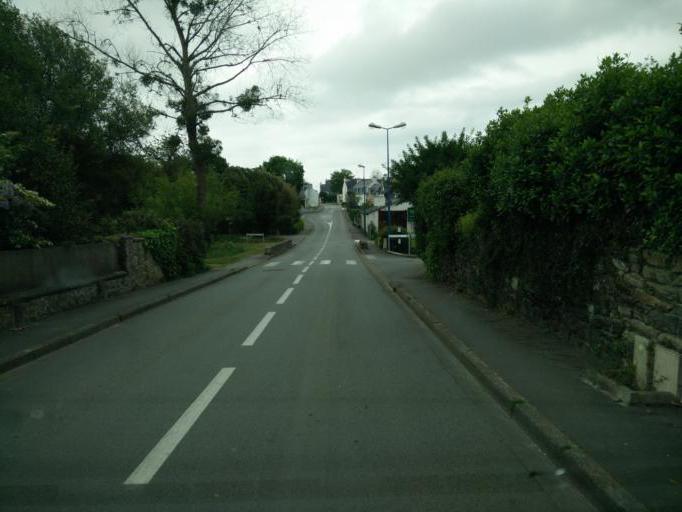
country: FR
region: Brittany
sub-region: Departement du Finistere
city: Tregunc
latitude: 47.8526
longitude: -3.8518
